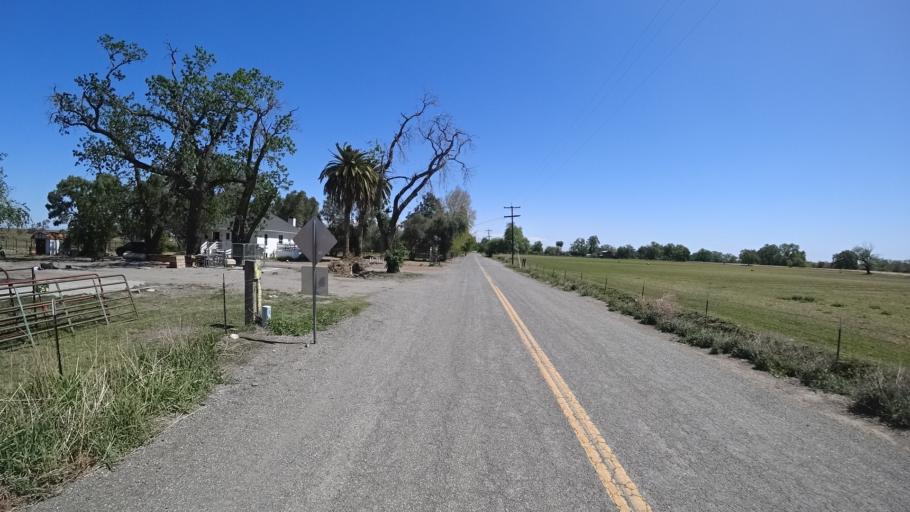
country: US
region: California
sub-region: Glenn County
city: Orland
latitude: 39.7952
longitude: -122.2495
